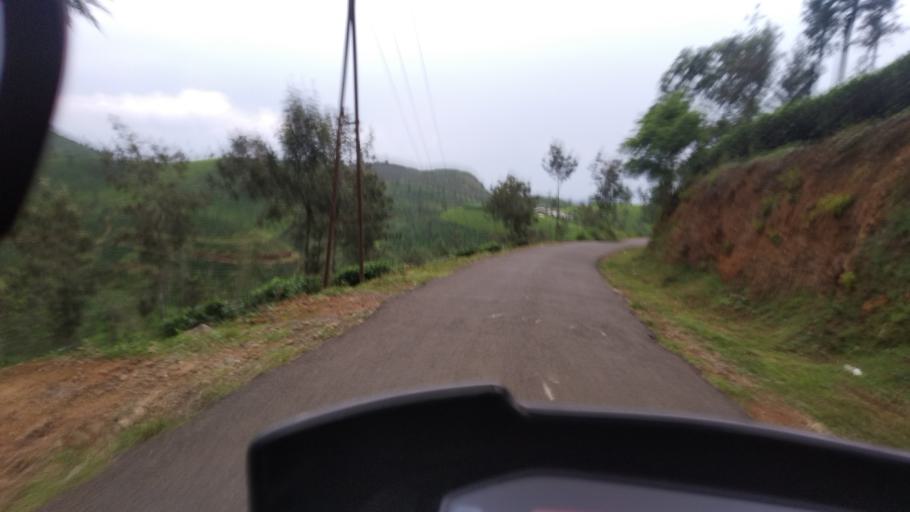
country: IN
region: Tamil Nadu
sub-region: Theni
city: Gudalur
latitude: 9.5407
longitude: 77.0430
